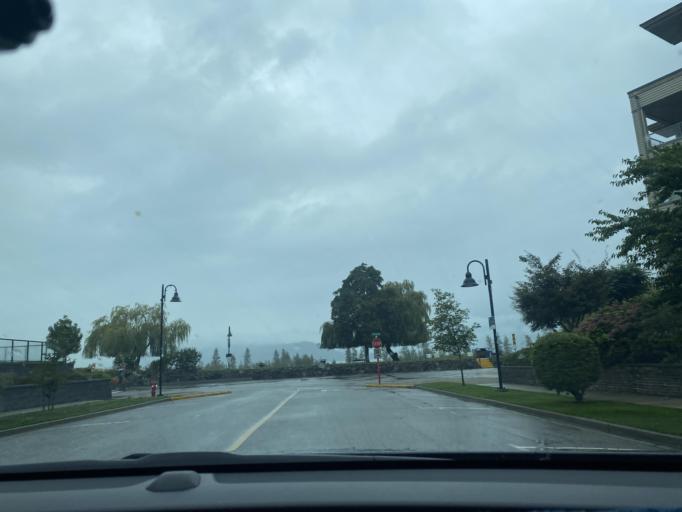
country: CA
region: British Columbia
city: Agassiz
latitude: 49.3027
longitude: -121.7798
